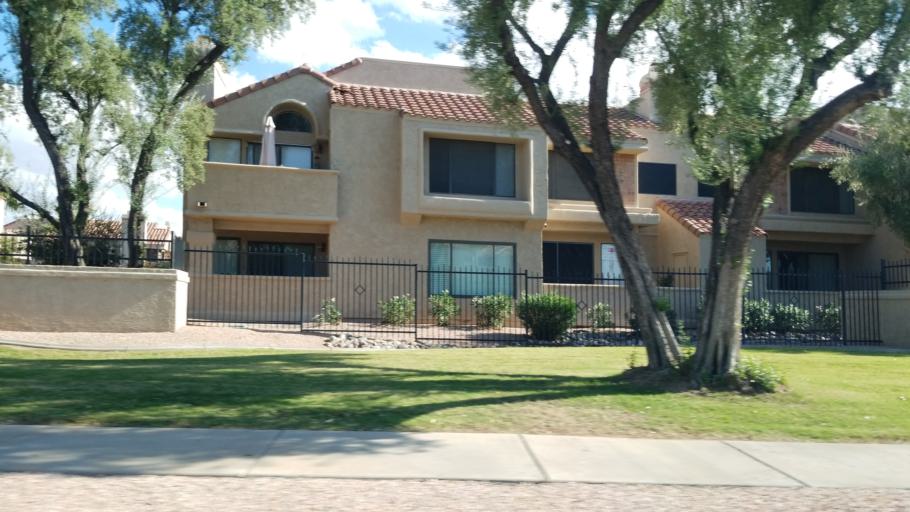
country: US
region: Arizona
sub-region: Maricopa County
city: Scottsdale
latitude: 33.5732
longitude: -111.8662
